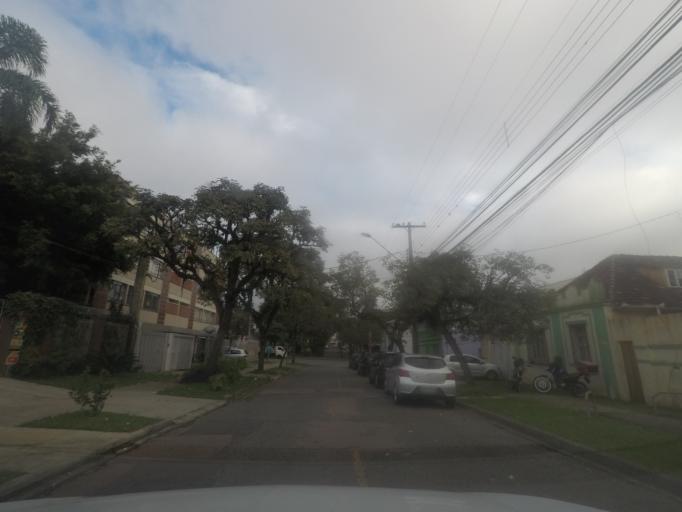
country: BR
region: Parana
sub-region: Curitiba
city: Curitiba
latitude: -25.4295
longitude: -49.2479
